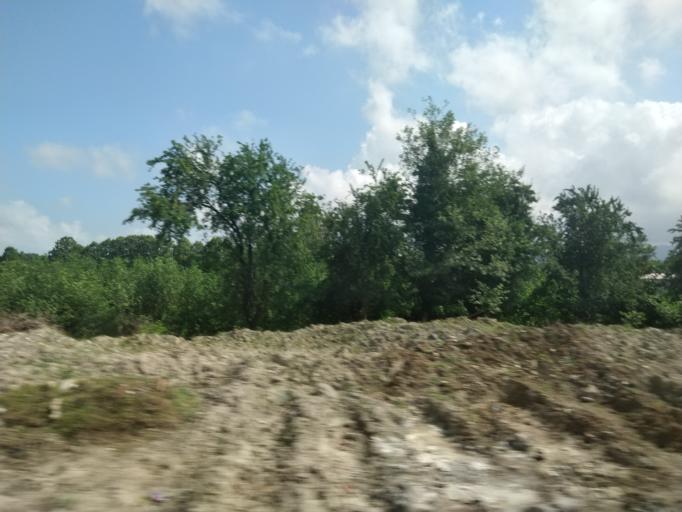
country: GE
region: Ajaria
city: Khelvachauri
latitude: 41.5844
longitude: 41.6042
